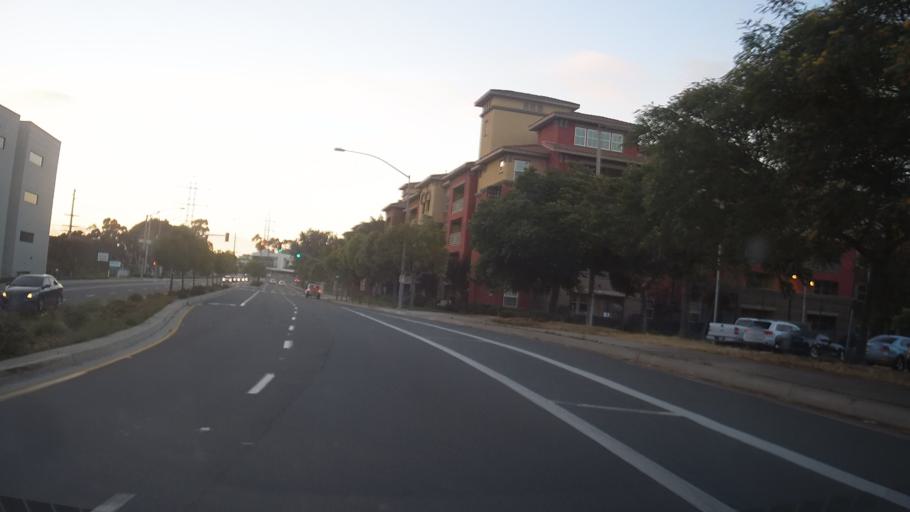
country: US
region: California
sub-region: San Diego County
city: San Diego
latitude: 32.8053
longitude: -117.1499
